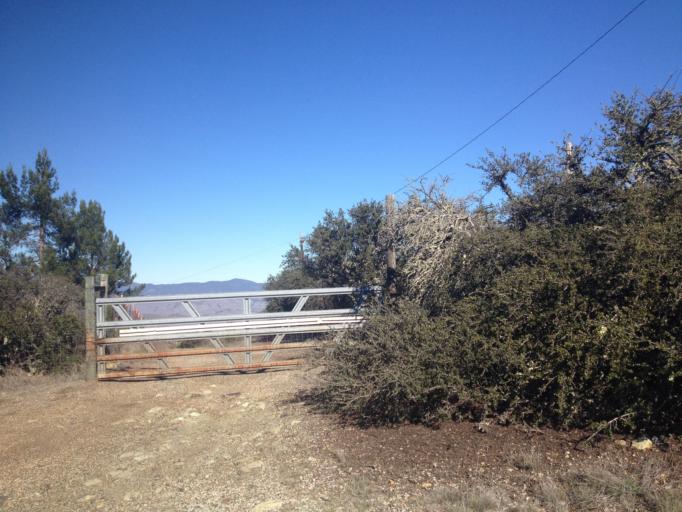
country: US
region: California
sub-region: San Luis Obispo County
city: Avila Beach
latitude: 35.2529
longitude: -120.7630
